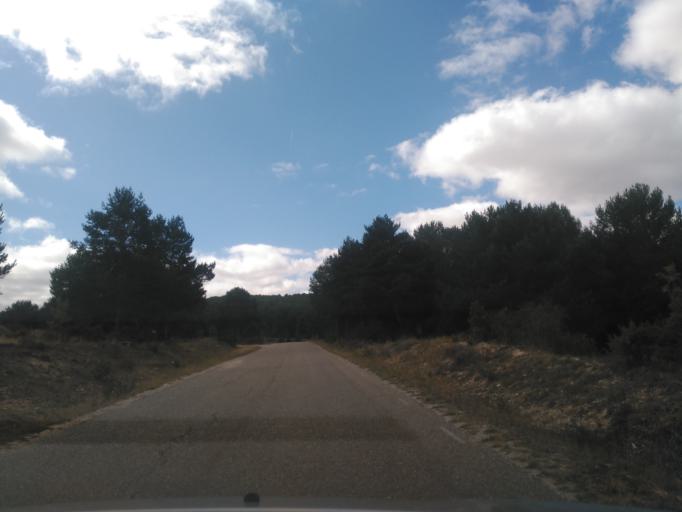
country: ES
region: Castille and Leon
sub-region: Provincia de Soria
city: Espejon
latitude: 41.8491
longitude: -3.2299
